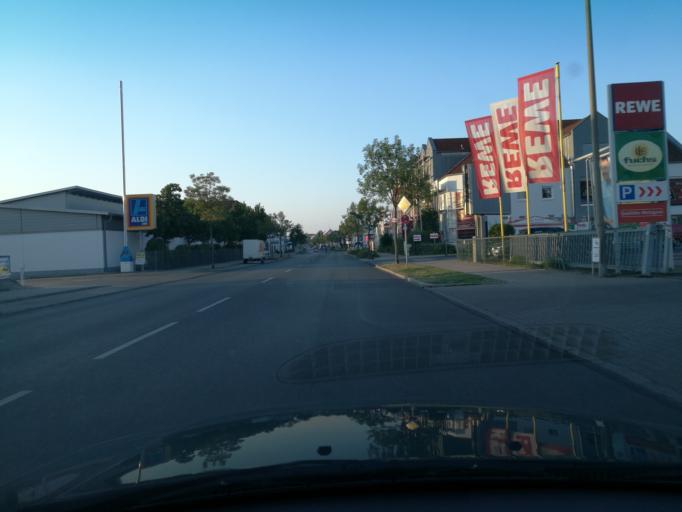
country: DE
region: Bavaria
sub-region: Regierungsbezirk Mittelfranken
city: Furth
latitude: 49.4816
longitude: 11.0088
